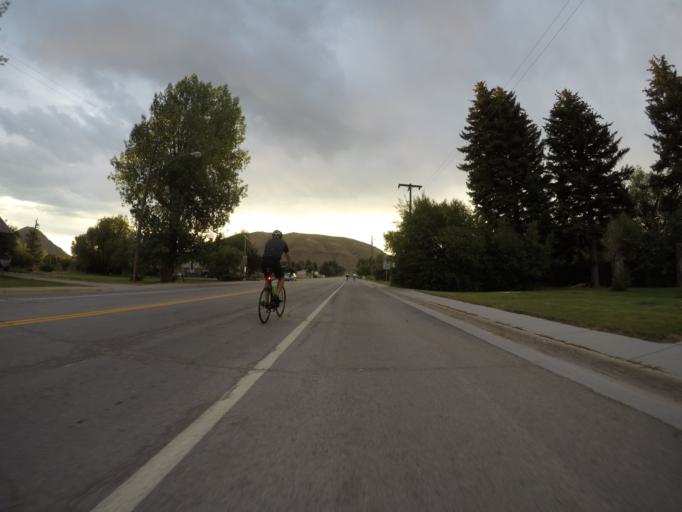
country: US
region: Idaho
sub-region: Bear Lake County
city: Montpelier
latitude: 42.0855
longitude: -110.9535
